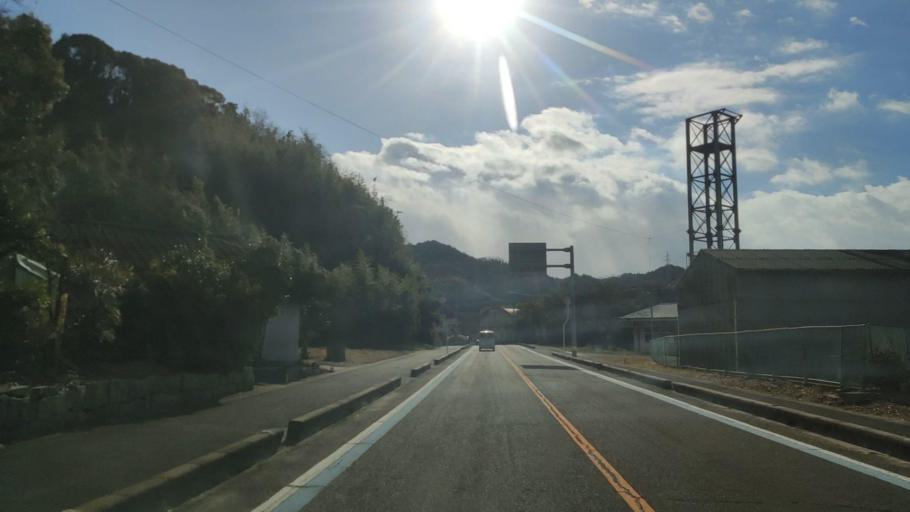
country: JP
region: Hiroshima
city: Innoshima
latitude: 34.2198
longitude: 133.0683
